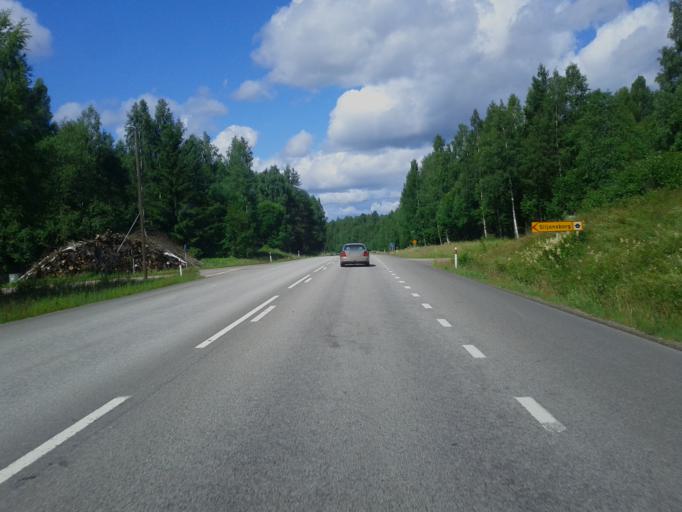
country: SE
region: Dalarna
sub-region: Rattviks Kommun
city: Raettvik
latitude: 60.9039
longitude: 15.0719
